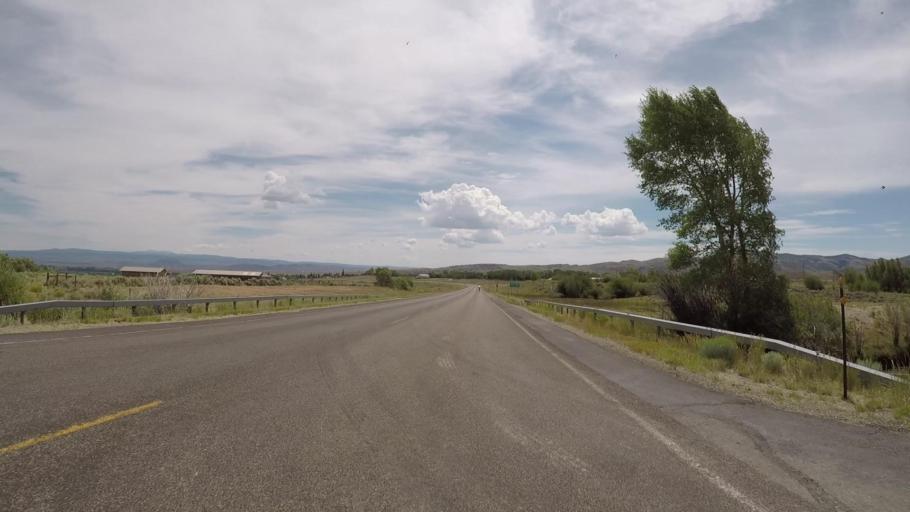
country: US
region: Wyoming
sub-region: Carbon County
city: Saratoga
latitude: 41.2045
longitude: -106.8078
